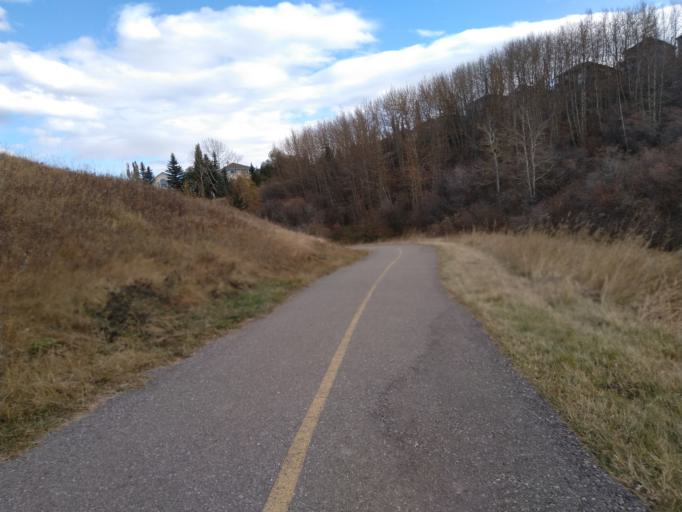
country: CA
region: Alberta
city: Calgary
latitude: 51.1363
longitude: -114.1392
